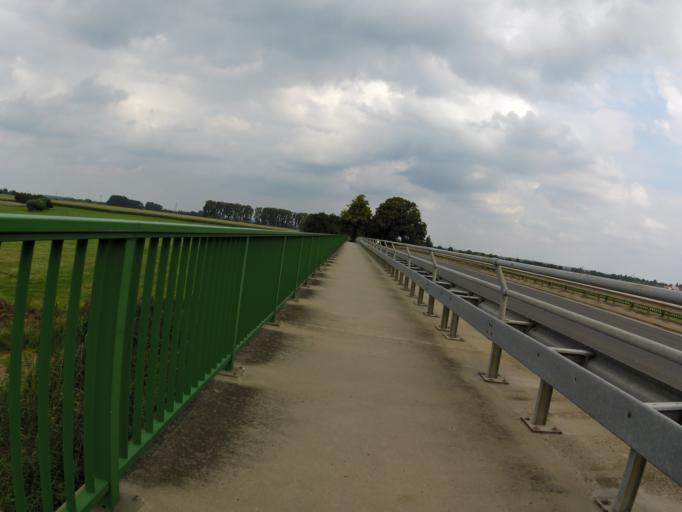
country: DE
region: Lower Saxony
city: Blender
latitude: 52.9210
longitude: 9.1661
